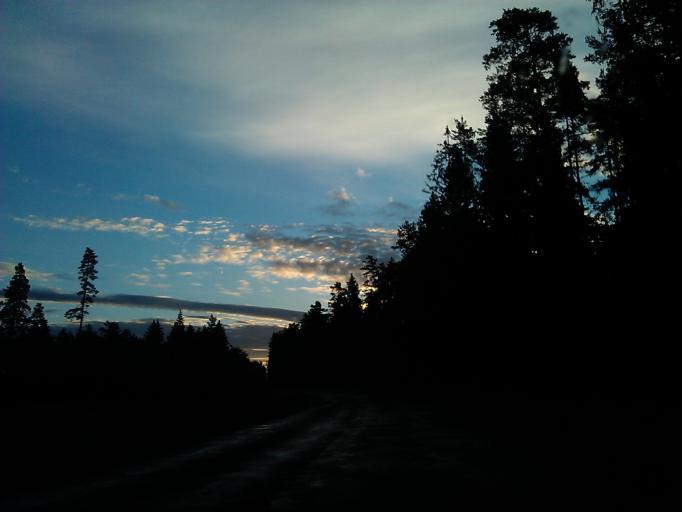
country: LV
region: Sigulda
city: Sigulda
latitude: 57.2426
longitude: 24.8630
